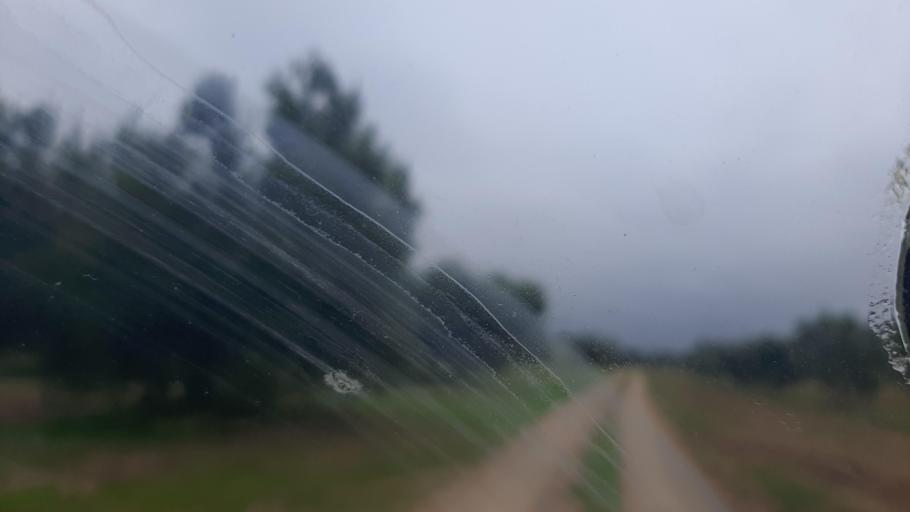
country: TN
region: Tunis
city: La Sebala du Mornag
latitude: 36.5791
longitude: 10.2902
